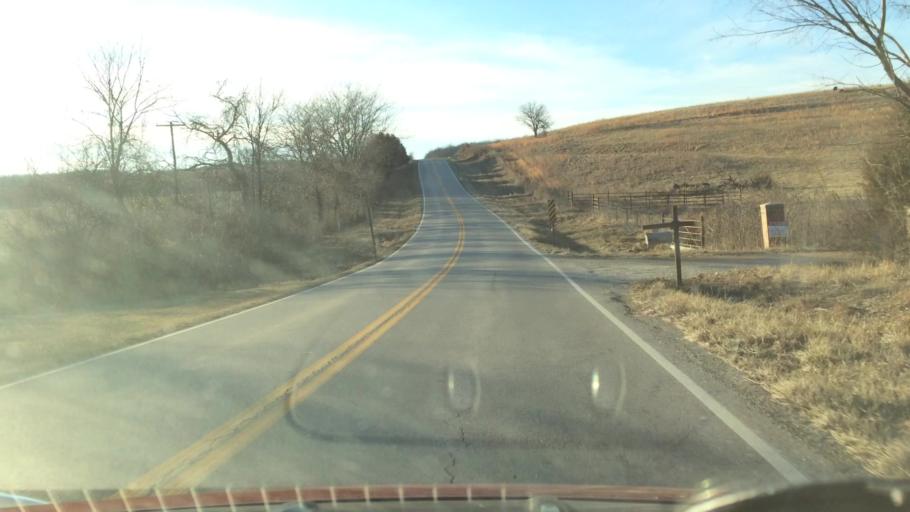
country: US
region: Missouri
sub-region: Webster County
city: Marshfield
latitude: 37.3407
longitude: -92.9651
